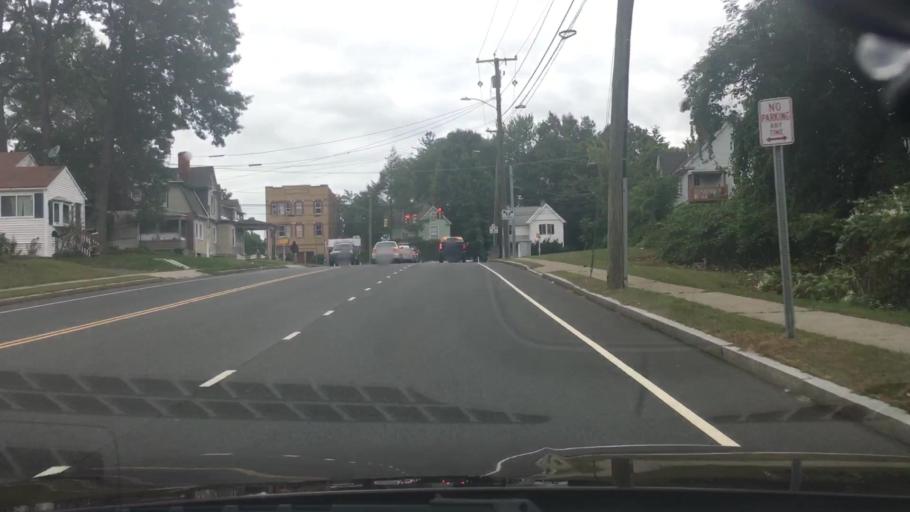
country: US
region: Connecticut
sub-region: Hartford County
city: East Hartford
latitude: 41.7772
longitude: -72.6201
